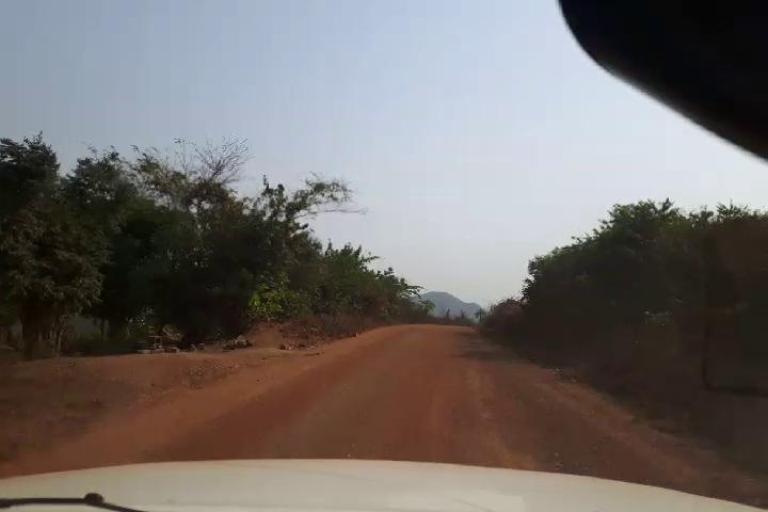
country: SL
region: Northern Province
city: Masingbi
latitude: 8.8561
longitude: -11.8243
